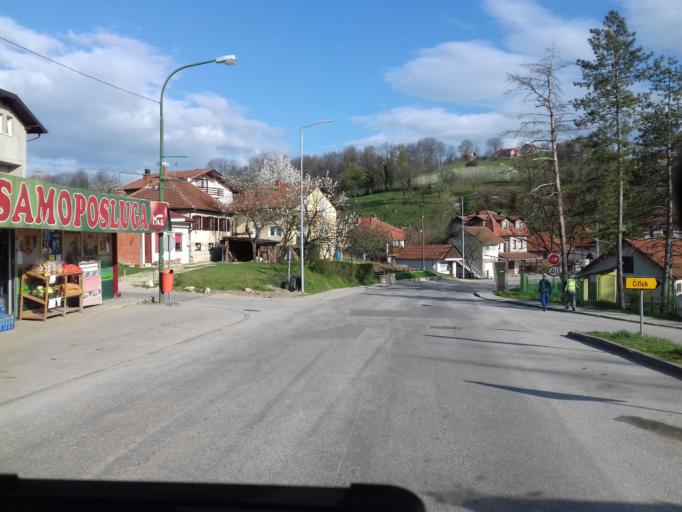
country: BA
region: Federation of Bosnia and Herzegovina
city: Tesanj
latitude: 44.6215
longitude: 17.9966
